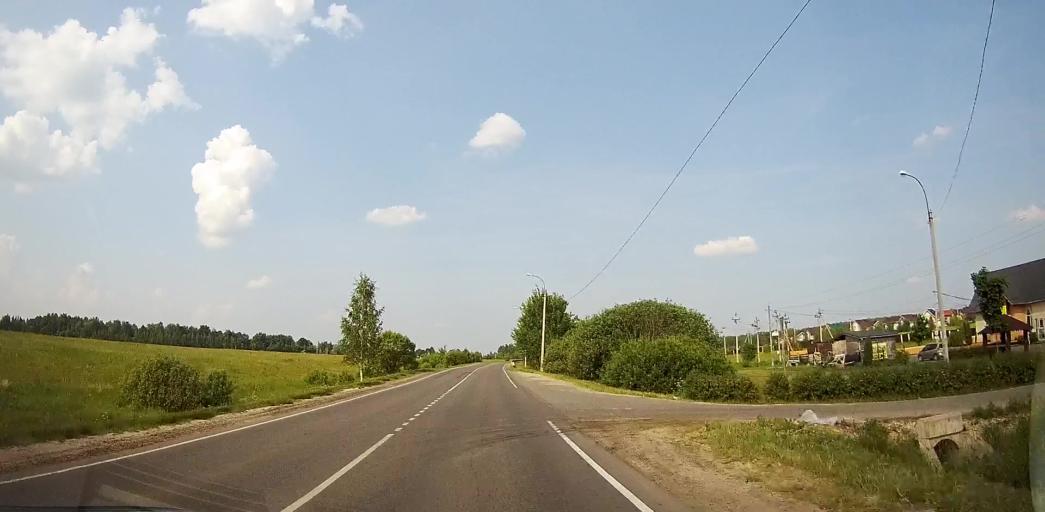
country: RU
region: Moskovskaya
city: Mikhnevo
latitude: 55.1752
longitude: 37.9664
